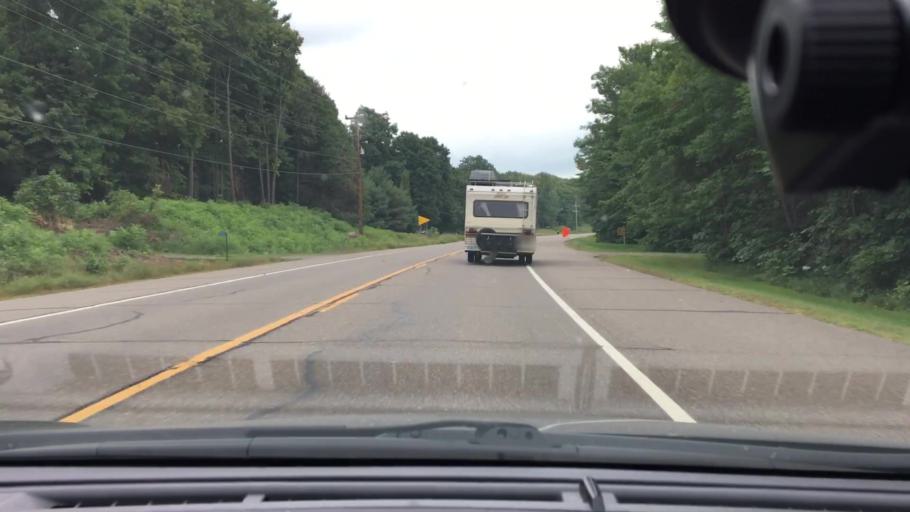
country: US
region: Minnesota
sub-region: Crow Wing County
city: Crosby
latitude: 46.4916
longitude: -93.9194
